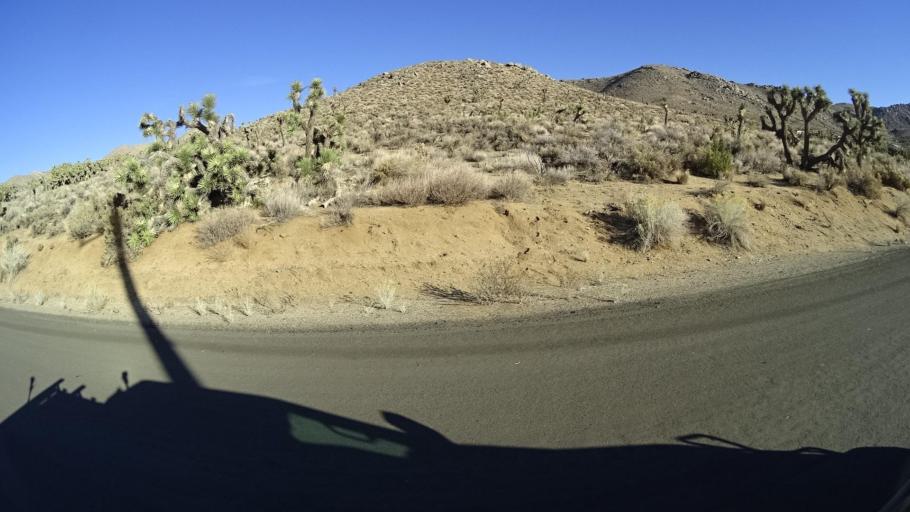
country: US
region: California
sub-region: Kern County
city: Weldon
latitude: 35.5188
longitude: -118.2038
